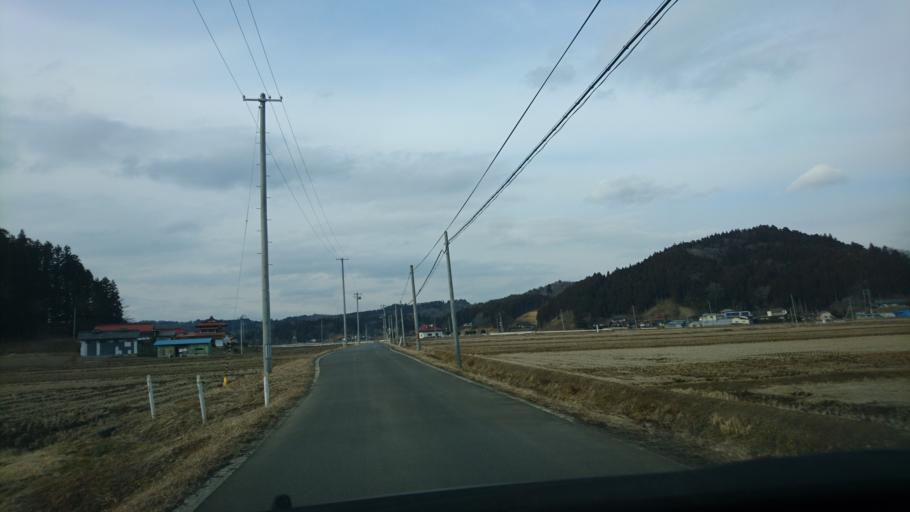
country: JP
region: Iwate
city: Ichinoseki
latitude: 38.8310
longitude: 141.2472
